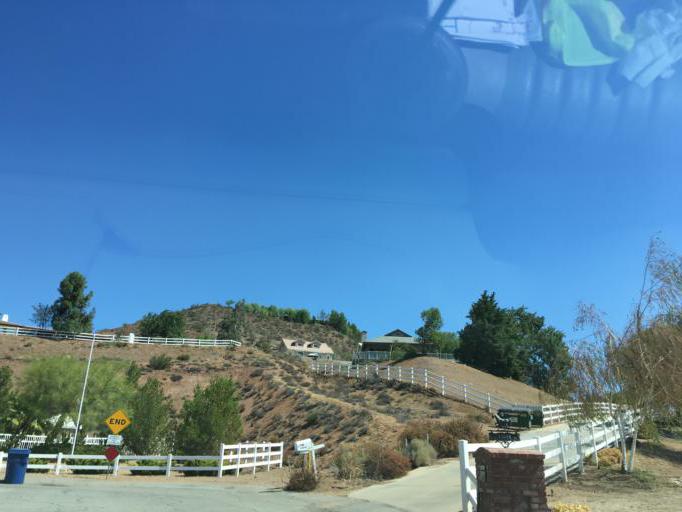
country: US
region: California
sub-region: Los Angeles County
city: Acton
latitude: 34.4959
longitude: -118.1620
